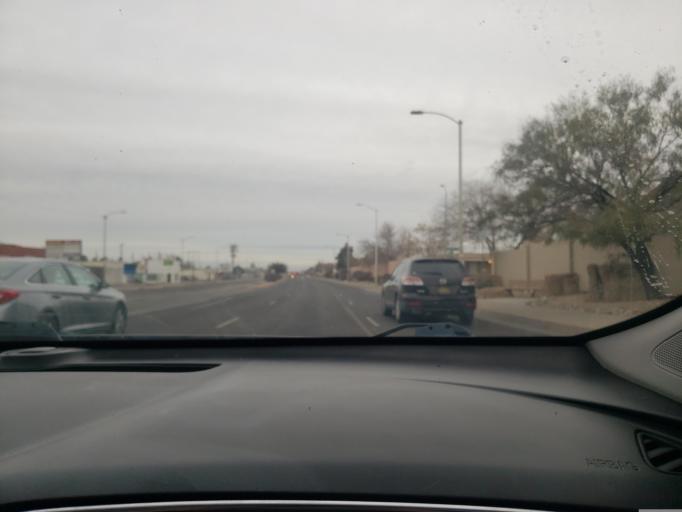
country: US
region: New Mexico
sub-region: Bernalillo County
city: Albuquerque
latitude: 35.0906
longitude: -106.5861
